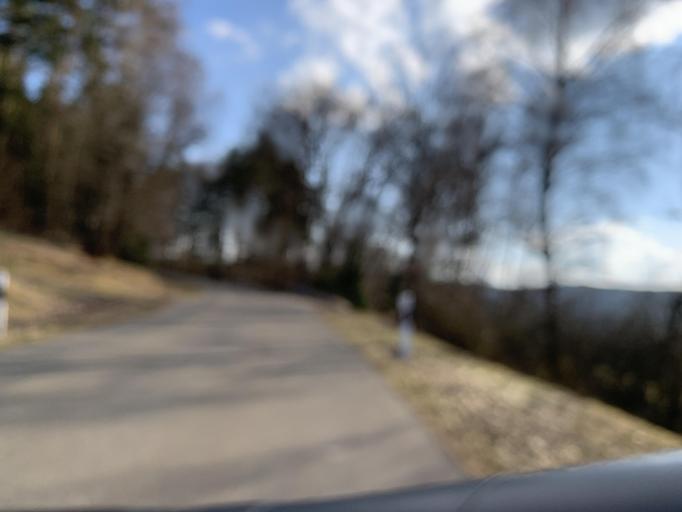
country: DE
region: Bavaria
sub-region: Upper Palatinate
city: Thanstein
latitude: 49.3734
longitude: 12.4348
